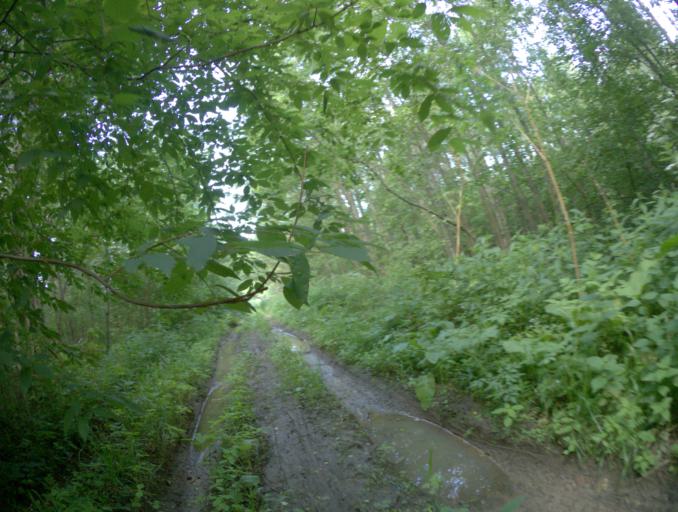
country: RU
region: Vladimir
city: Stavrovo
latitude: 56.3188
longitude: 39.9487
